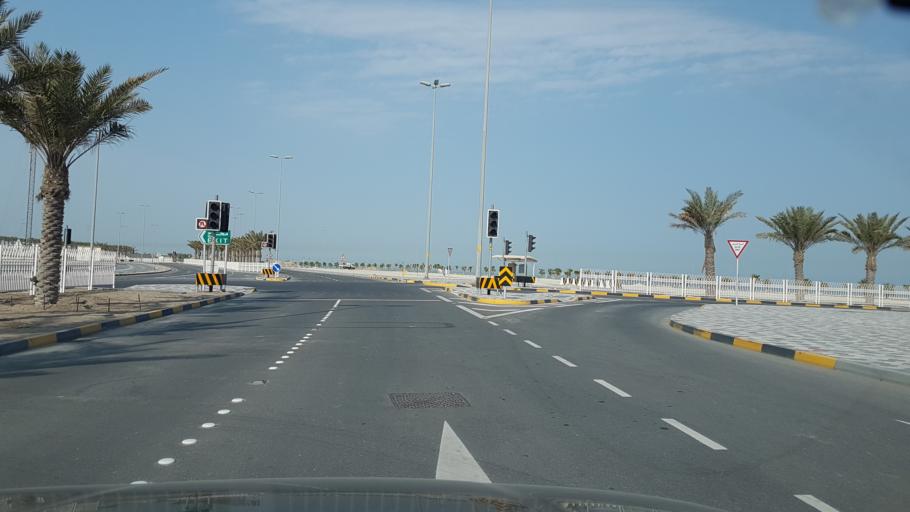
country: BH
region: Muharraq
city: Al Hadd
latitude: 26.2710
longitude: 50.6776
